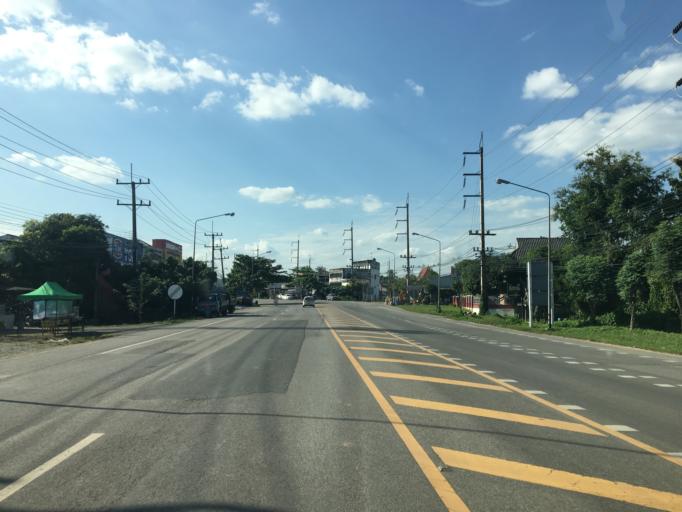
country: TH
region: Phayao
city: Chun
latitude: 19.3382
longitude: 100.1308
